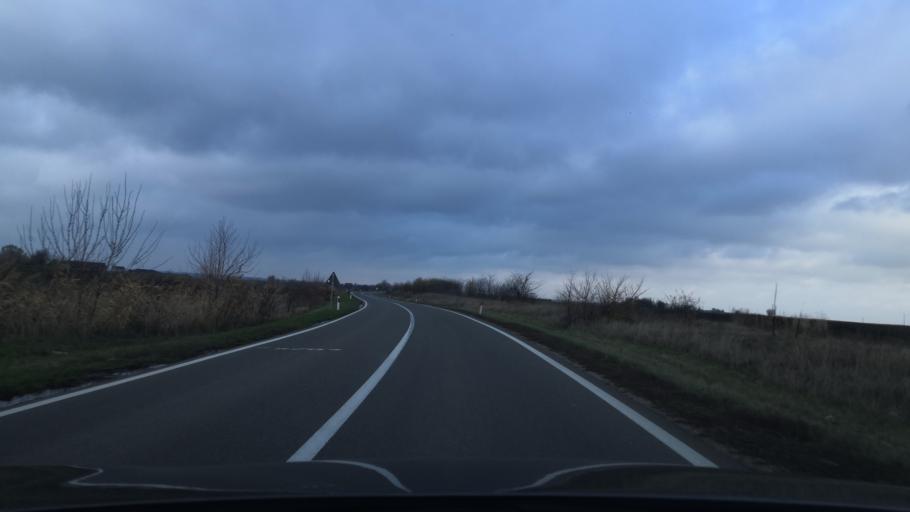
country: RS
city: Sanad
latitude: 45.9877
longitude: 20.1104
